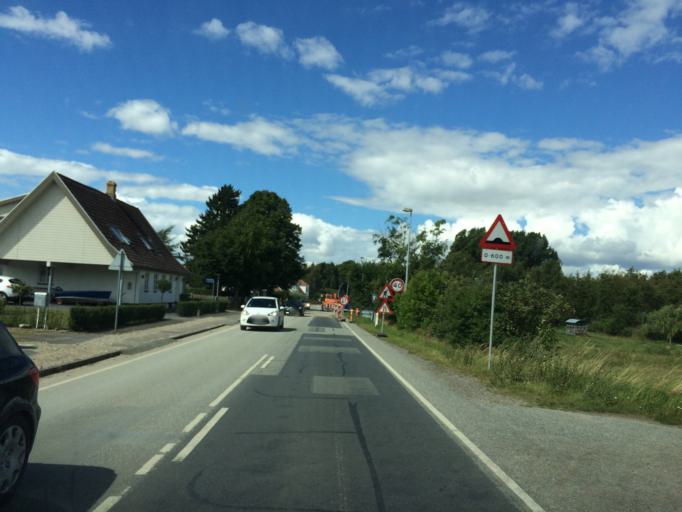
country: DK
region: South Denmark
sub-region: Assens Kommune
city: Harby
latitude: 55.1504
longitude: 10.1511
